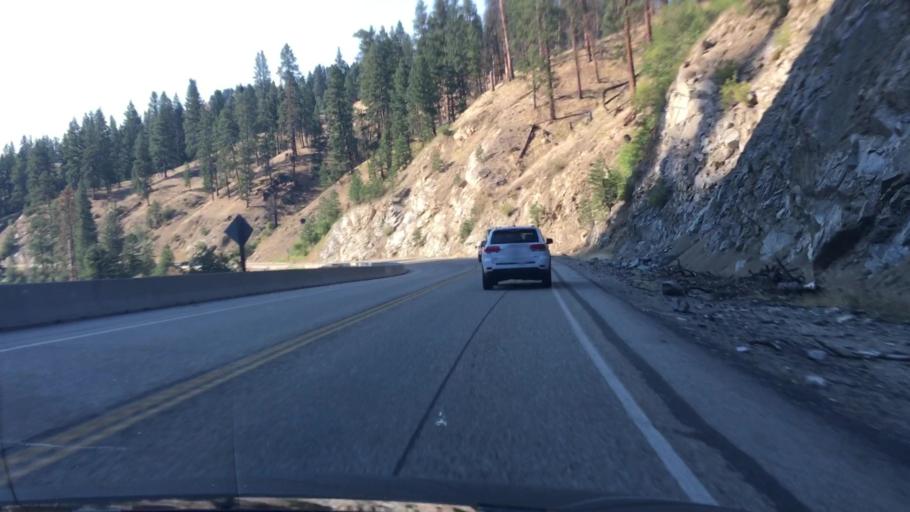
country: US
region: Idaho
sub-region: Boise County
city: Idaho City
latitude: 44.1056
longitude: -116.0951
